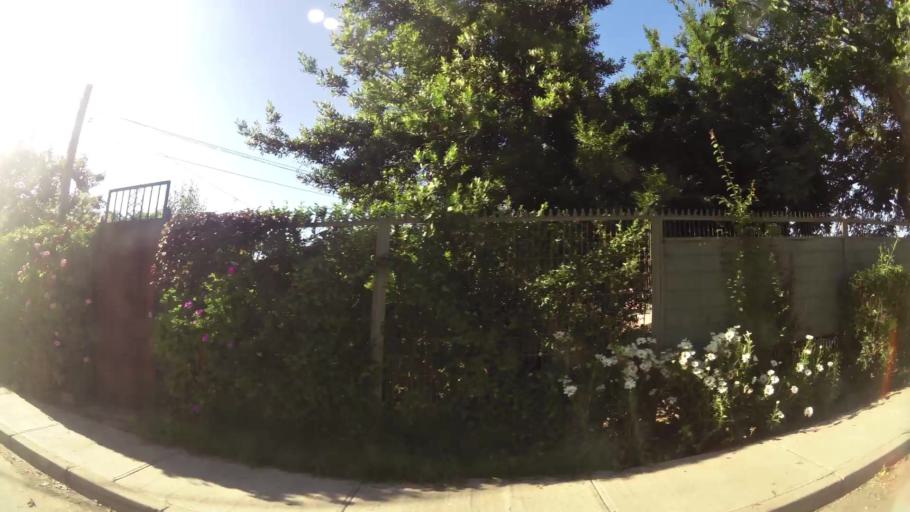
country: CL
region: Santiago Metropolitan
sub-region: Provincia de Maipo
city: San Bernardo
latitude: -33.6422
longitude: -70.7075
